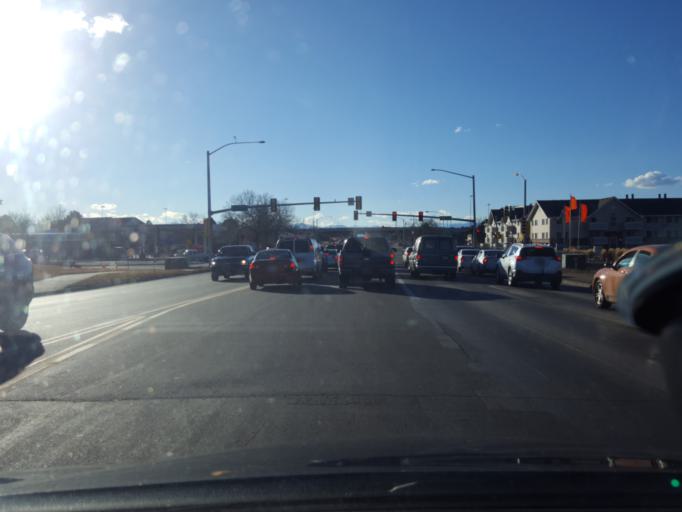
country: US
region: Colorado
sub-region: Adams County
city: Aurora
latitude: 39.7256
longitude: -104.8183
